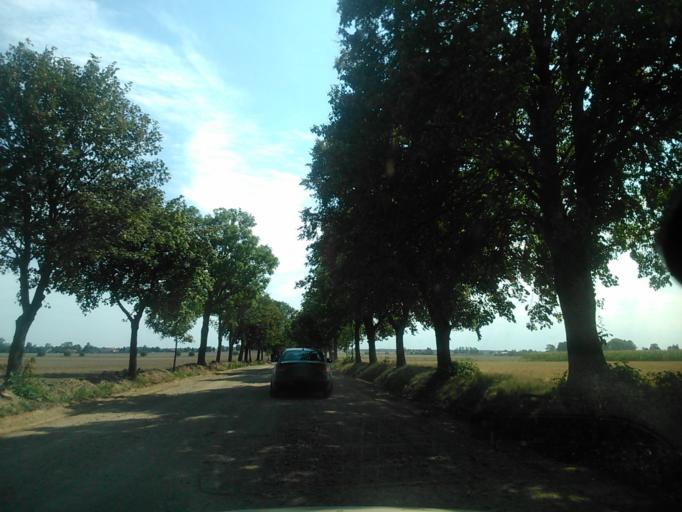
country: PL
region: Warmian-Masurian Voivodeship
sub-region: Powiat dzialdowski
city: Dzialdowo
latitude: 53.2139
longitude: 20.2229
